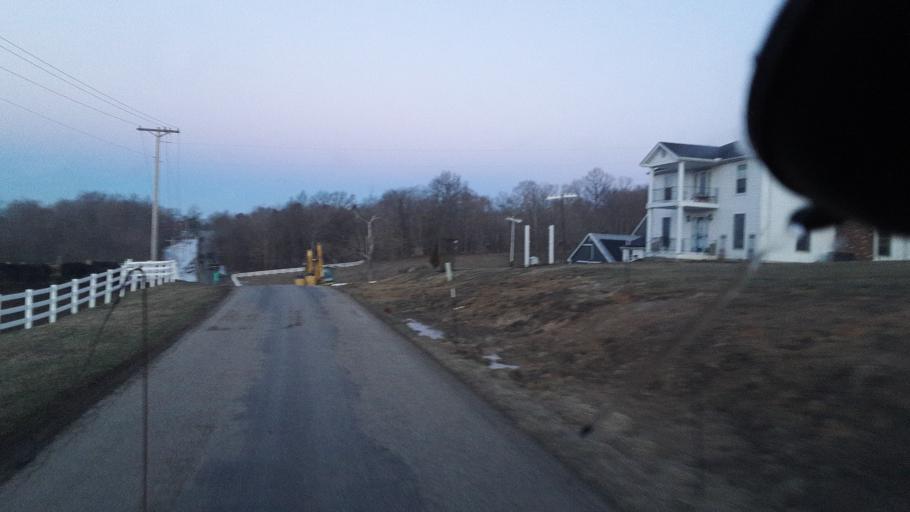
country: US
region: Ohio
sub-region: Fairfield County
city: Bremen
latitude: 39.7065
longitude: -82.3274
